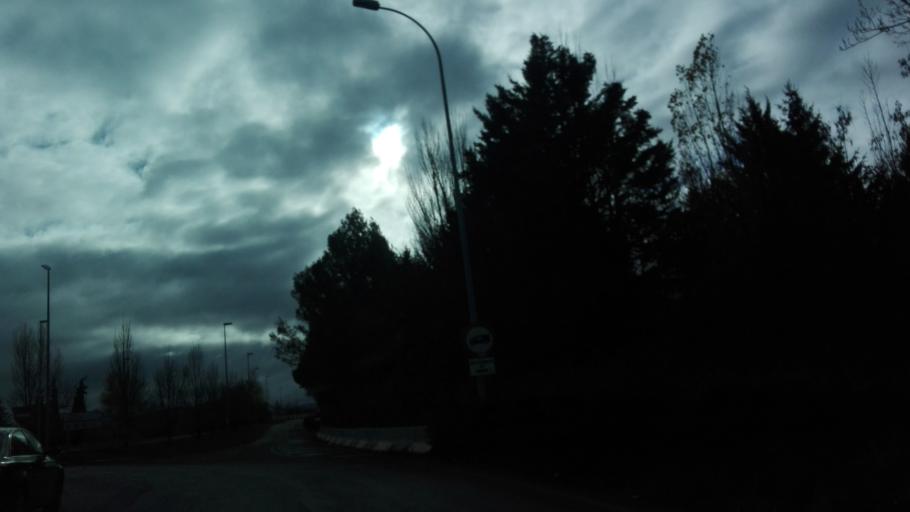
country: ES
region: Navarre
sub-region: Provincia de Navarra
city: Egues-Uharte
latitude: 42.8260
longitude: -1.5849
